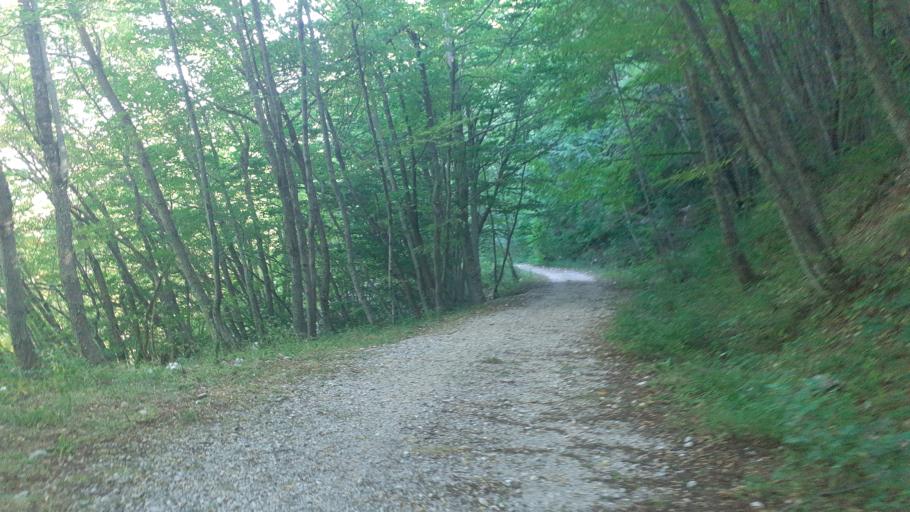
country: IT
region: Abruzzo
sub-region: Provincia di Pescara
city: Sant'Eufemia a Maiella
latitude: 42.1095
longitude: 13.9992
